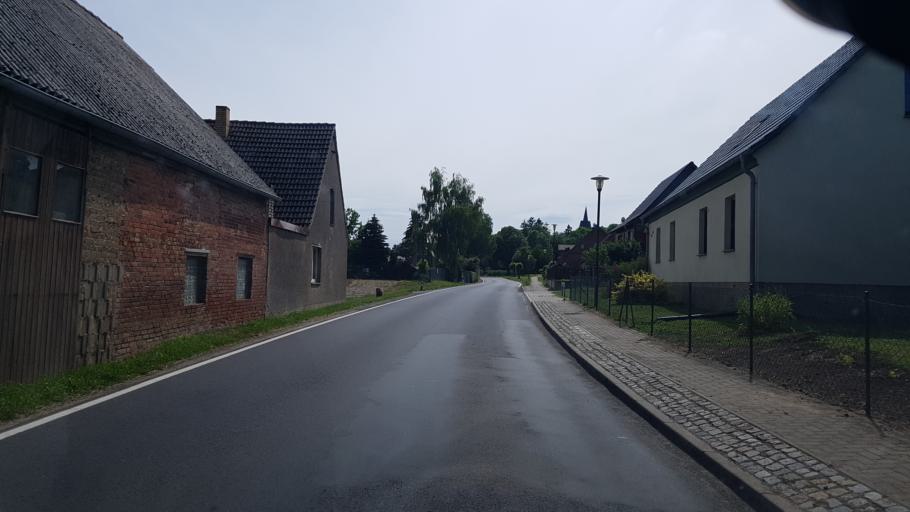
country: DE
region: Brandenburg
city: Prenzlau
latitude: 53.3254
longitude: 13.7903
